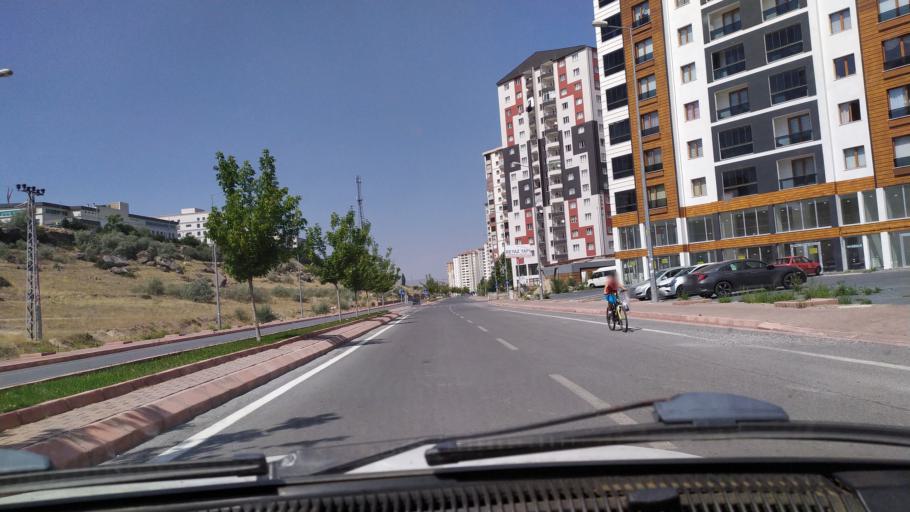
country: TR
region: Kayseri
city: Talas
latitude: 38.7102
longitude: 35.5568
